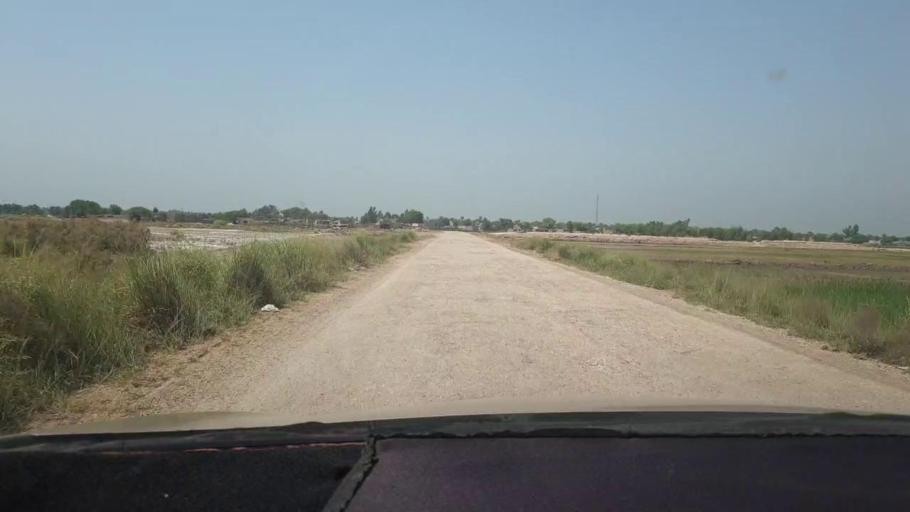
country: PK
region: Sindh
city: Miro Khan
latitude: 27.6663
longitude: 68.0682
